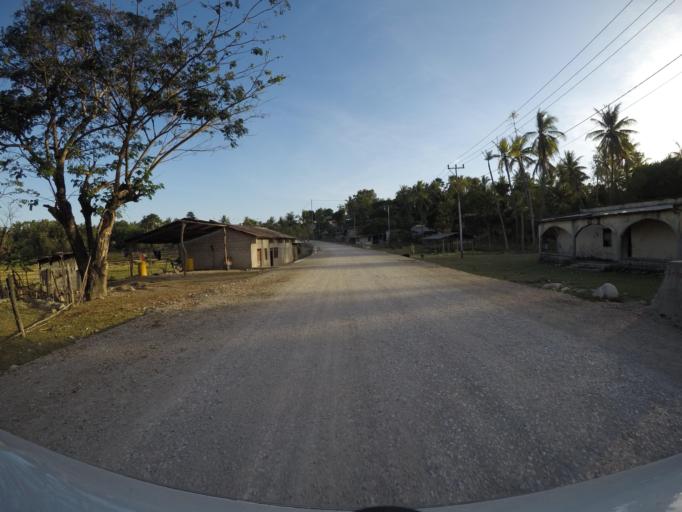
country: TL
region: Viqueque
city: Viqueque
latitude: -8.8192
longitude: 126.5332
